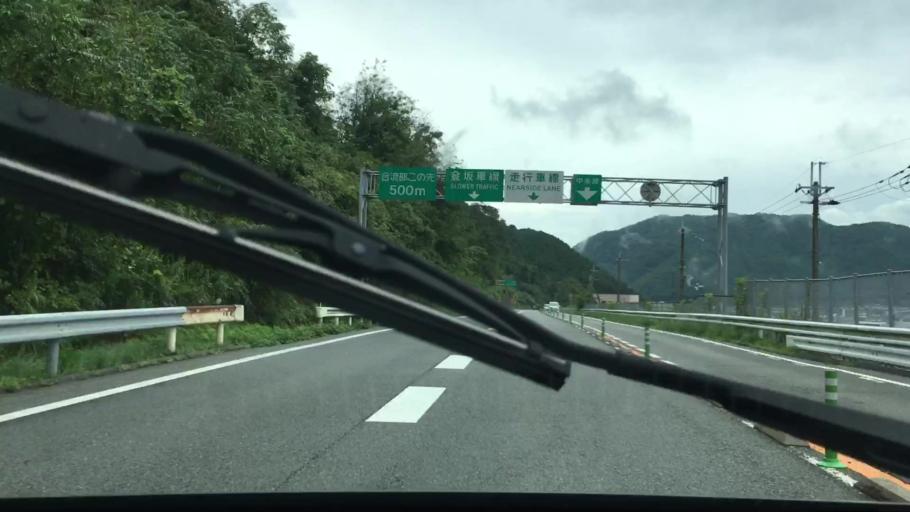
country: JP
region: Hyogo
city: Himeji
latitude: 34.9992
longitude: 134.7681
